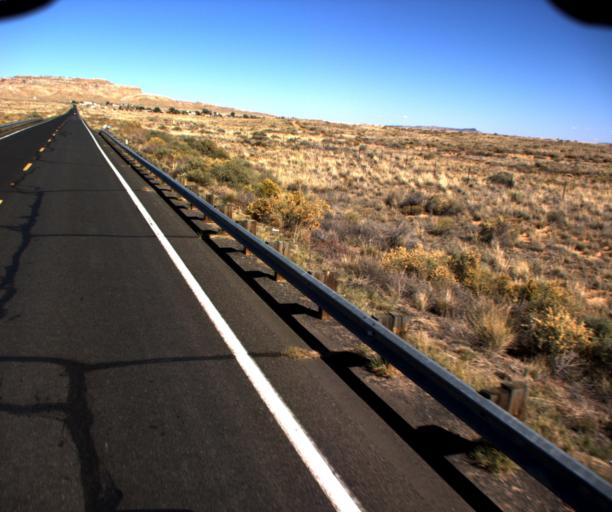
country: US
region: Arizona
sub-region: Navajo County
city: First Mesa
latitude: 35.7740
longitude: -110.5046
